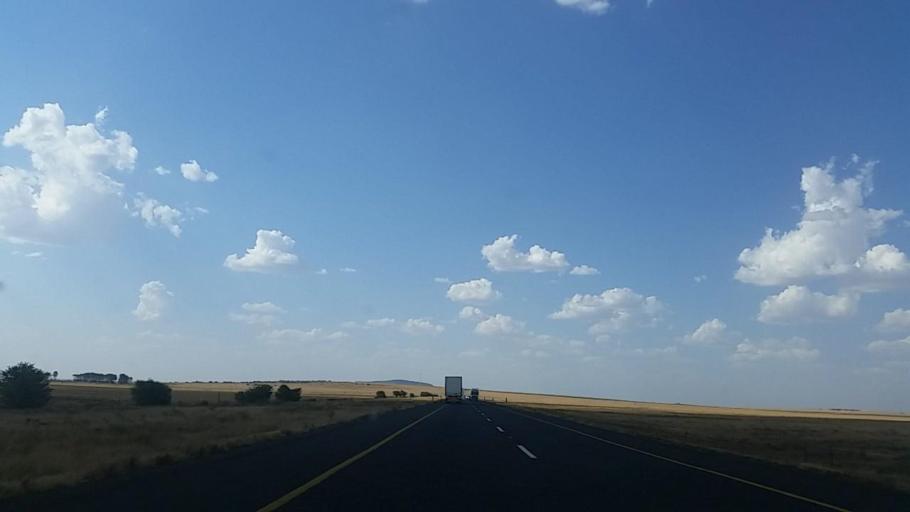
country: ZA
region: Orange Free State
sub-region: Mangaung Metropolitan Municipality
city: Bloemfontein
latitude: -29.3475
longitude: 26.1513
